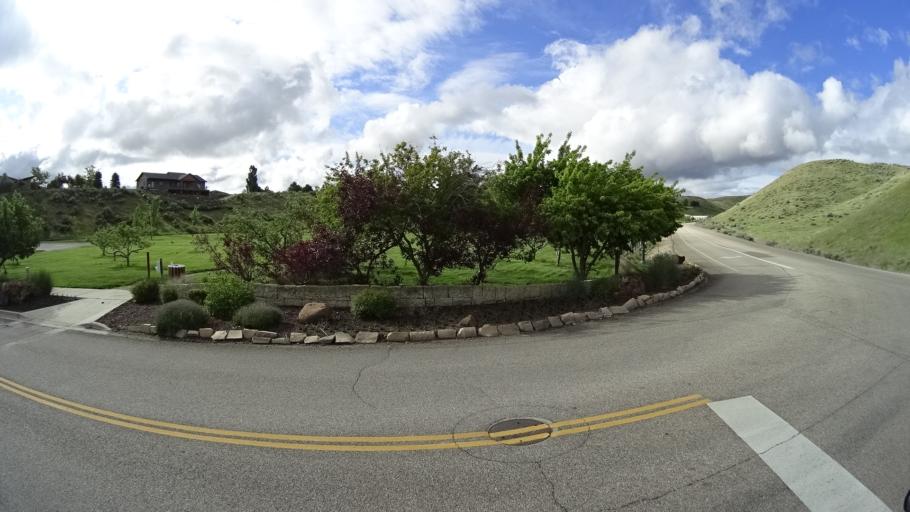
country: US
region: Idaho
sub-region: Ada County
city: Eagle
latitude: 43.7249
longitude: -116.2624
